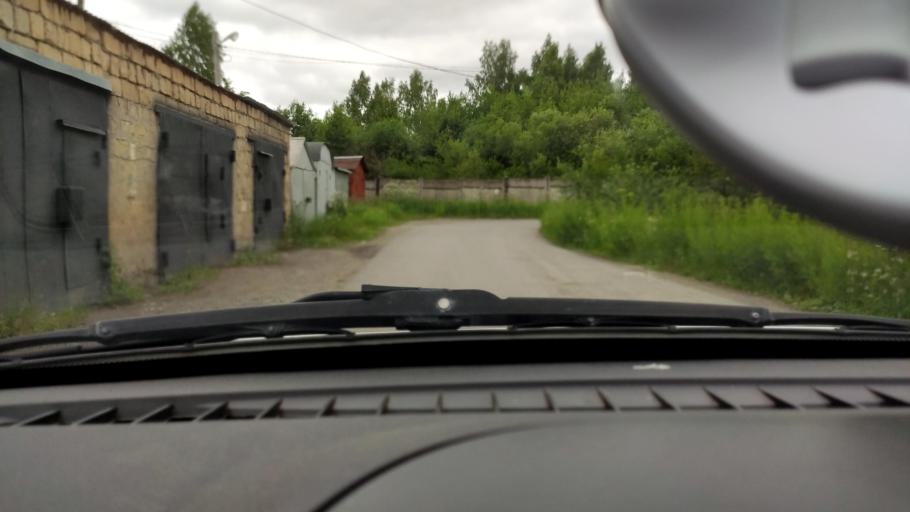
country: RU
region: Perm
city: Ferma
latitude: 57.8876
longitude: 56.2973
